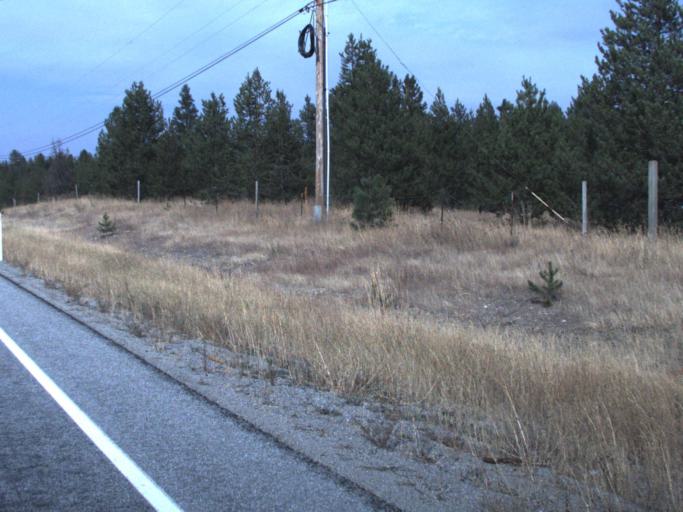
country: US
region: Washington
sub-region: Pend Oreille County
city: Newport
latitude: 48.1855
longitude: -117.3016
